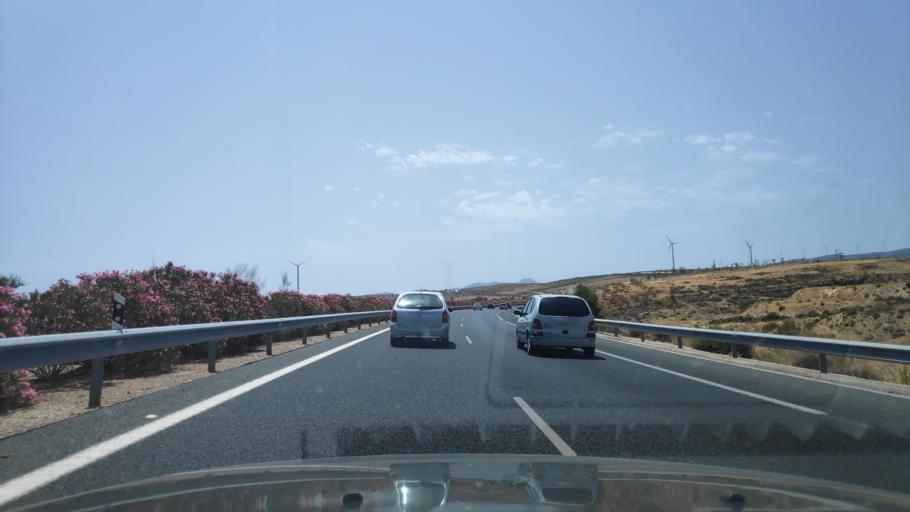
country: ES
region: Andalusia
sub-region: Provincia de Granada
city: Padul
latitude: 37.0180
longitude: -3.6406
